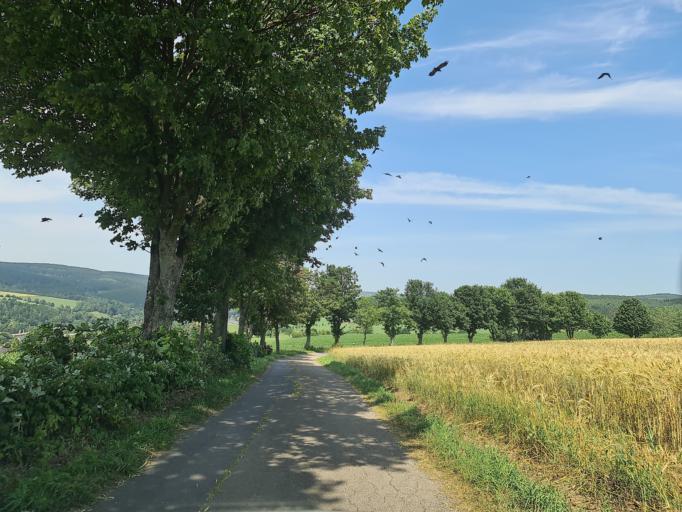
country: DE
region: Saxony
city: Neuhausen
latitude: 50.6664
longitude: 13.4705
